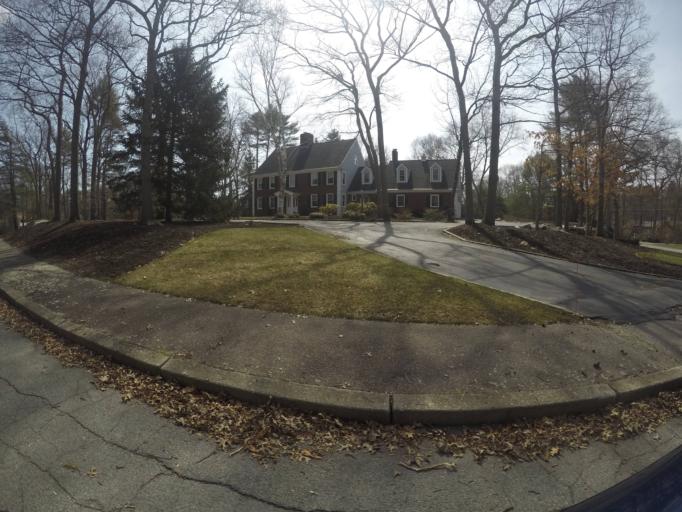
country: US
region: Massachusetts
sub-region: Bristol County
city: Easton
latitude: 42.0523
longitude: -71.1258
